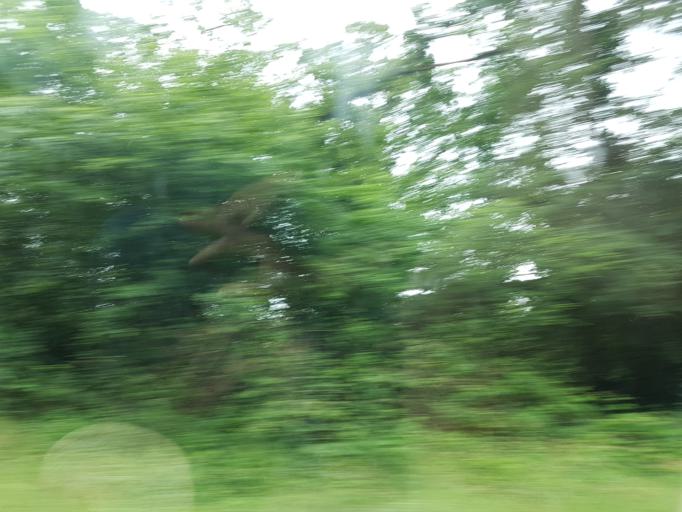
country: FR
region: Bourgogne
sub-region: Departement de la Nievre
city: Corbigny
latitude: 47.1945
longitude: 3.7251
